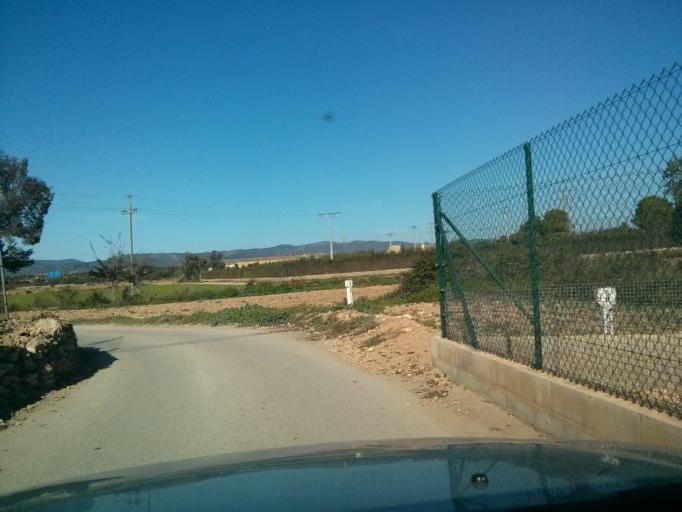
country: ES
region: Catalonia
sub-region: Provincia de Tarragona
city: Santa Oliva
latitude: 41.2514
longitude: 1.5418
